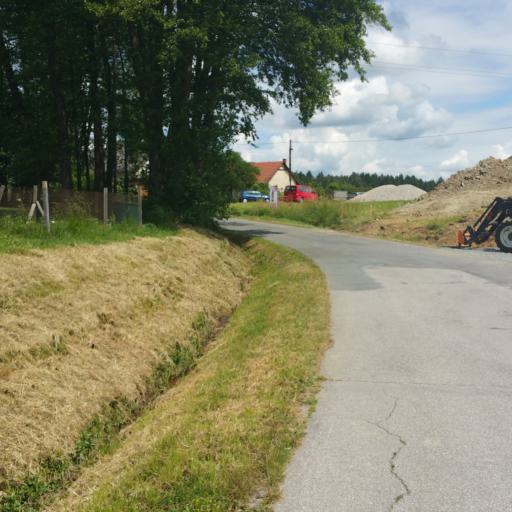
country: AT
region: Styria
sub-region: Politischer Bezirk Leibnitz
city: Gleinstatten
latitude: 46.7451
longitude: 15.3431
